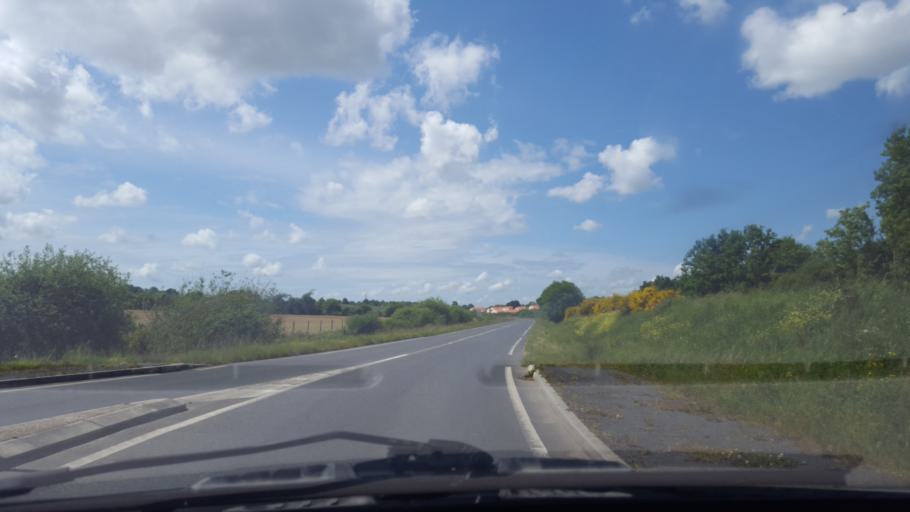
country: FR
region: Pays de la Loire
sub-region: Departement de la Loire-Atlantique
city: Saint-Philbert-de-Grand-Lieu
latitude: 47.0302
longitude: -1.6479
